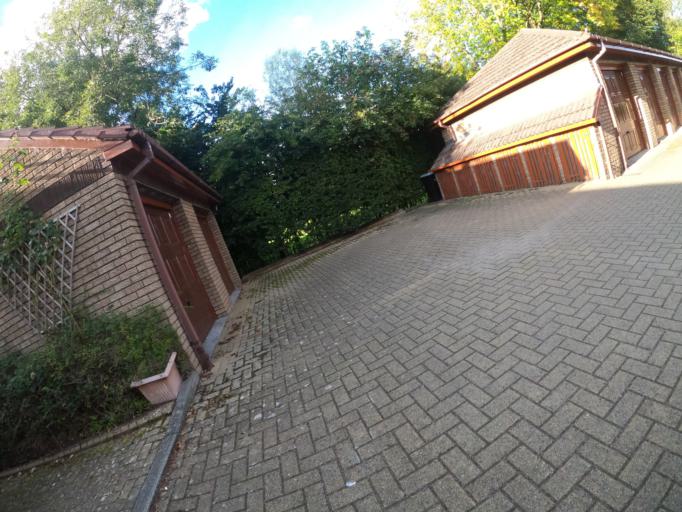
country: GB
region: Scotland
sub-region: Edinburgh
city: Currie
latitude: 55.9622
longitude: -3.3017
